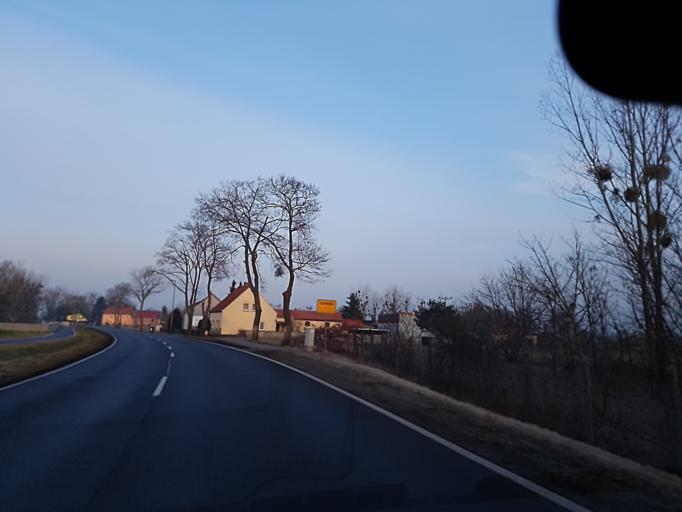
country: DE
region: Saxony-Anhalt
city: Elster
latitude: 51.8355
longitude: 12.7938
